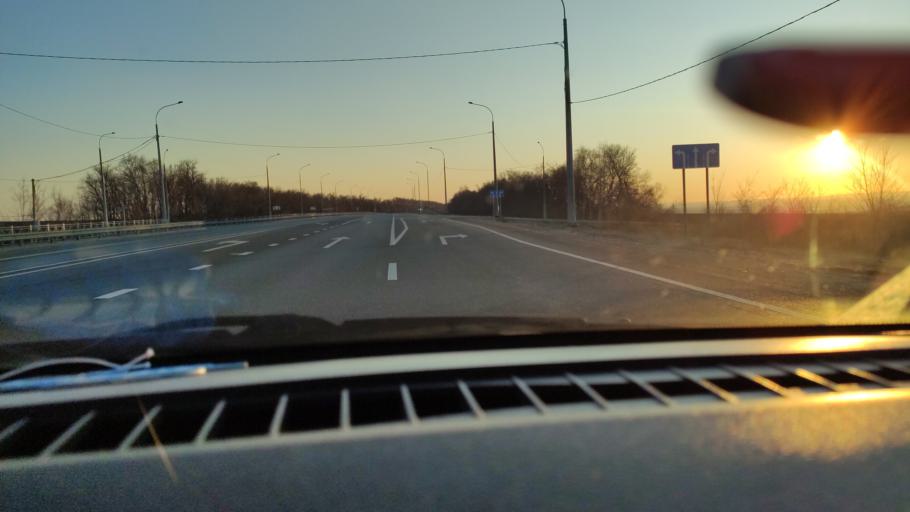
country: RU
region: Saratov
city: Yelshanka
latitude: 51.8944
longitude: 46.5285
